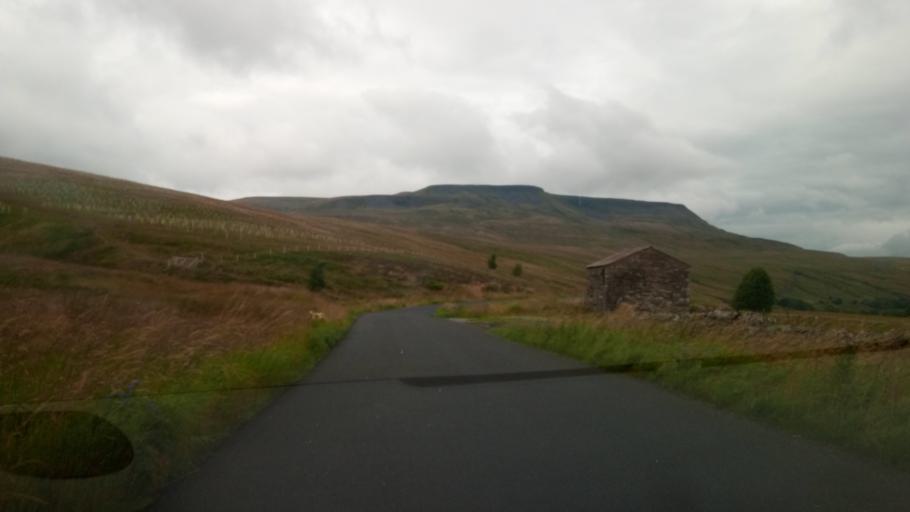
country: GB
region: England
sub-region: Cumbria
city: Kirkby Stephen
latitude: 54.3634
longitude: -2.3461
